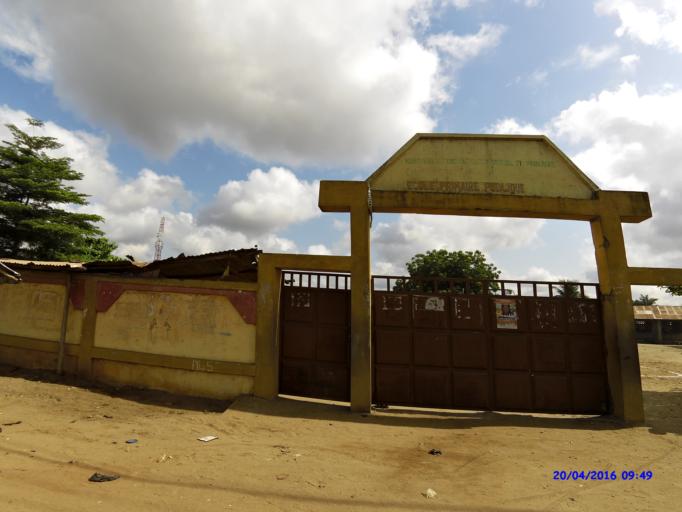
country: BJ
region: Atlantique
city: Hevie
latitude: 6.3885
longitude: 2.3016
